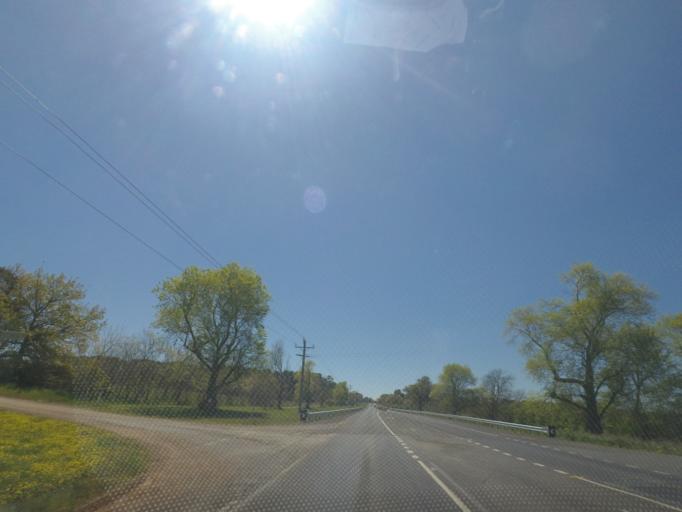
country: AU
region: Victoria
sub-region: Hume
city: Sunbury
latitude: -37.3398
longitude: 144.7417
